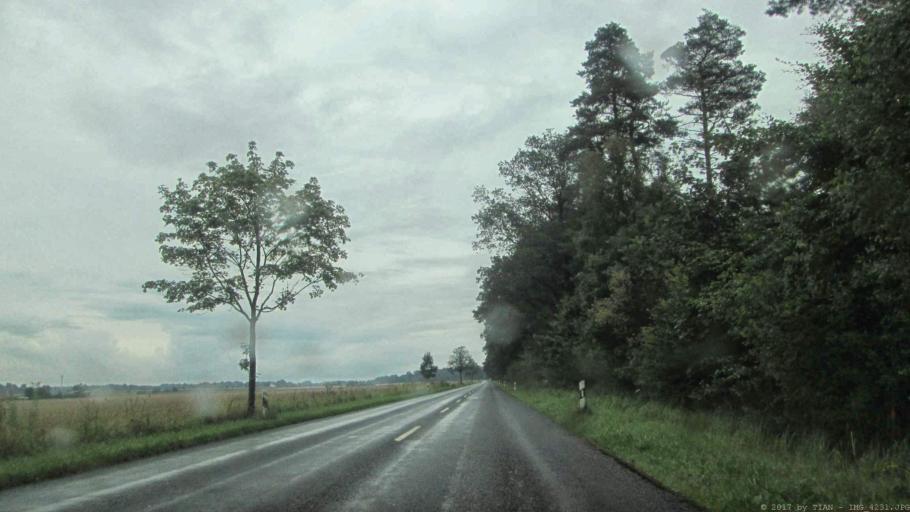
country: DE
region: Lower Saxony
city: Danndorf
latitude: 52.4180
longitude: 10.8855
